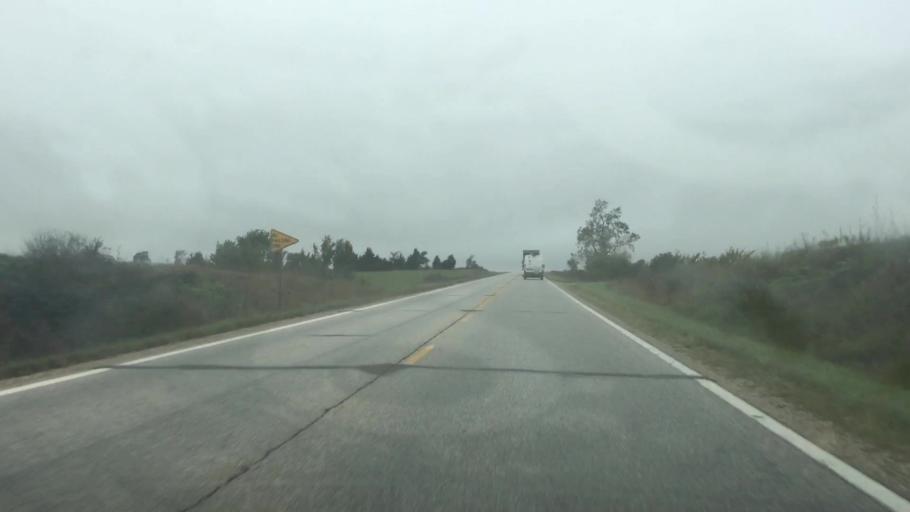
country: US
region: Kansas
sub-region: Anderson County
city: Garnett
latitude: 38.1778
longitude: -95.2698
